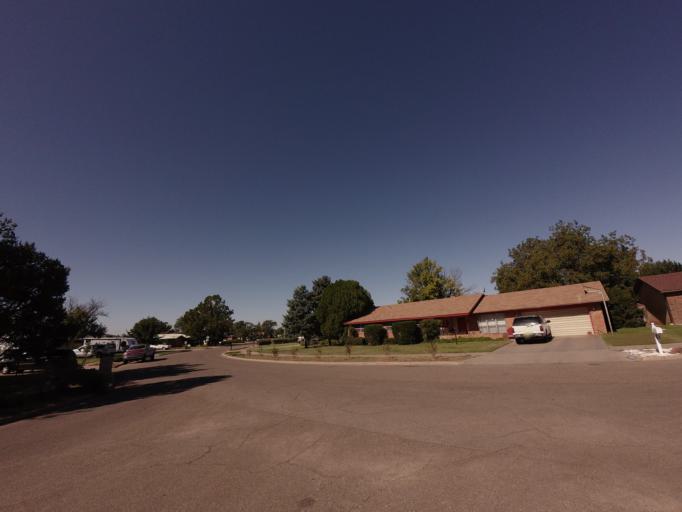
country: US
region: New Mexico
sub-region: Curry County
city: Clovis
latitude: 34.4230
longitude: -103.1835
